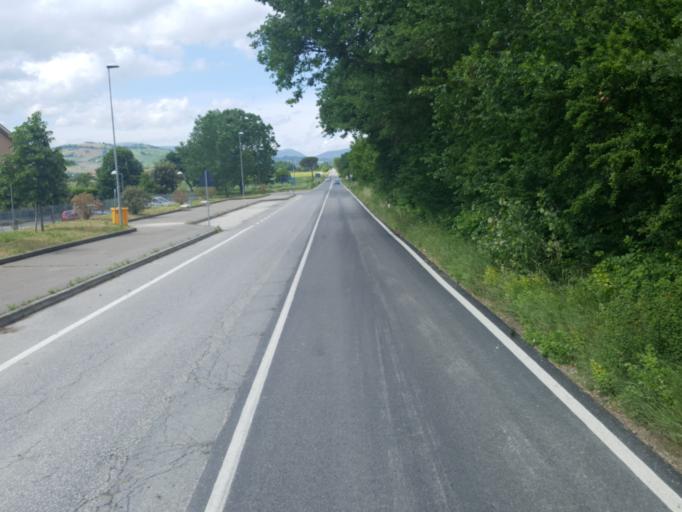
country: IT
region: The Marches
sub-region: Provincia di Macerata
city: Pollenza
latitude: 43.2393
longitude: 13.3673
